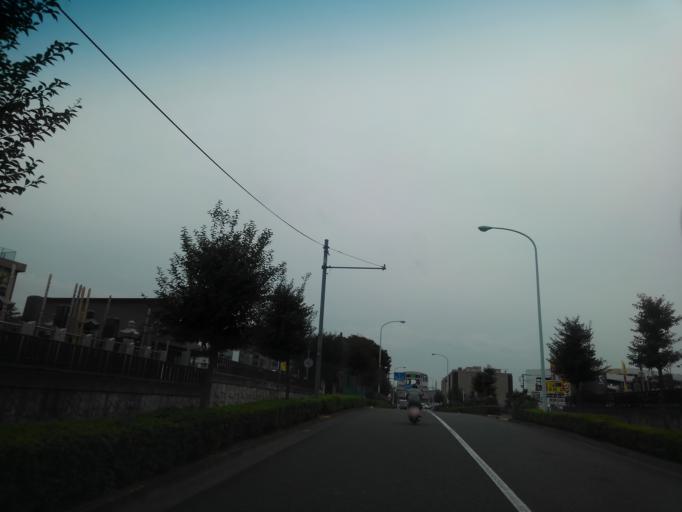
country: JP
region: Tokyo
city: Higashimurayama-shi
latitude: 35.7487
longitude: 139.4159
